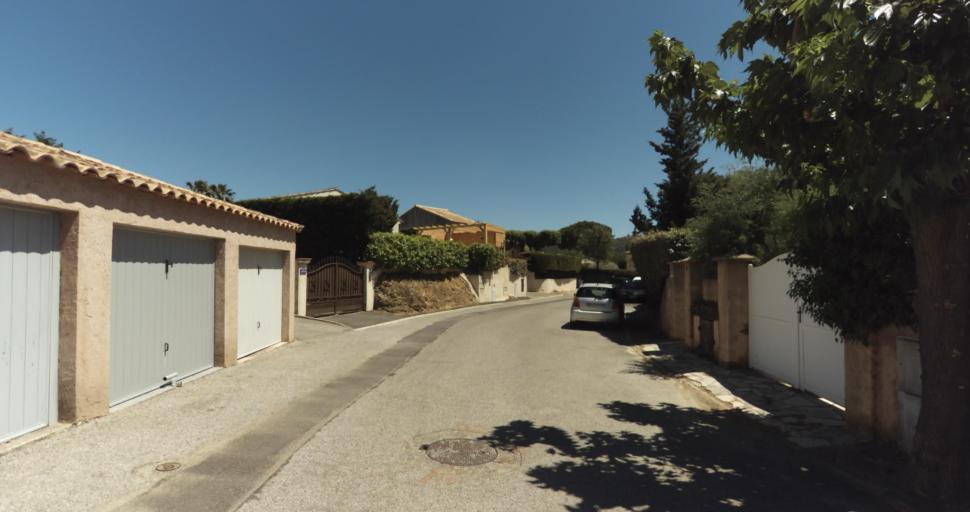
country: FR
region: Provence-Alpes-Cote d'Azur
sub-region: Departement du Var
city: Gassin
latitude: 43.2452
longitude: 6.5673
